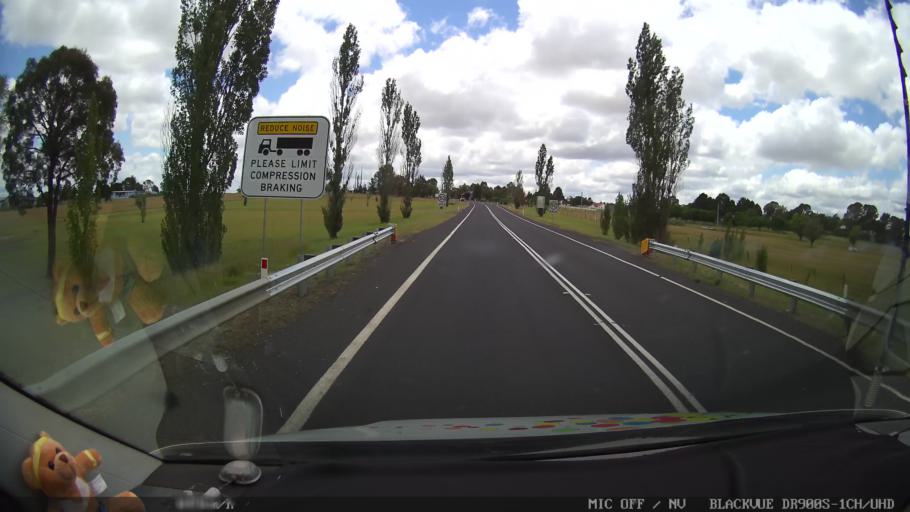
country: AU
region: New South Wales
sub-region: Glen Innes Severn
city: Glen Innes
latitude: -29.4455
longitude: 151.8439
